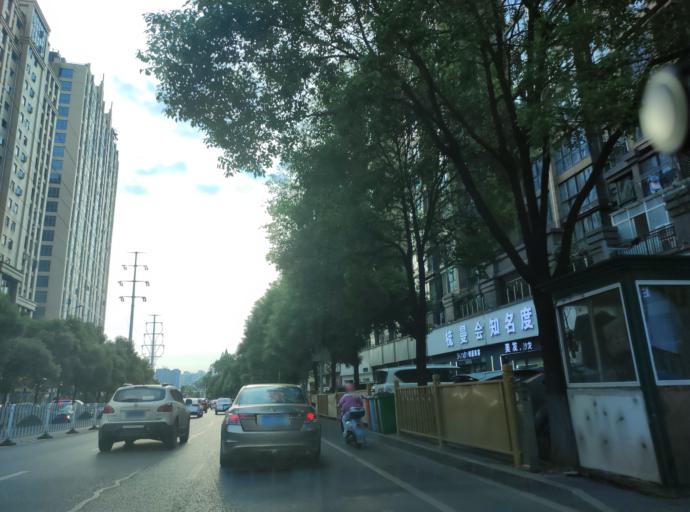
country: CN
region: Jiangxi Sheng
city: Pingxiang
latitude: 27.6337
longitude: 113.8662
